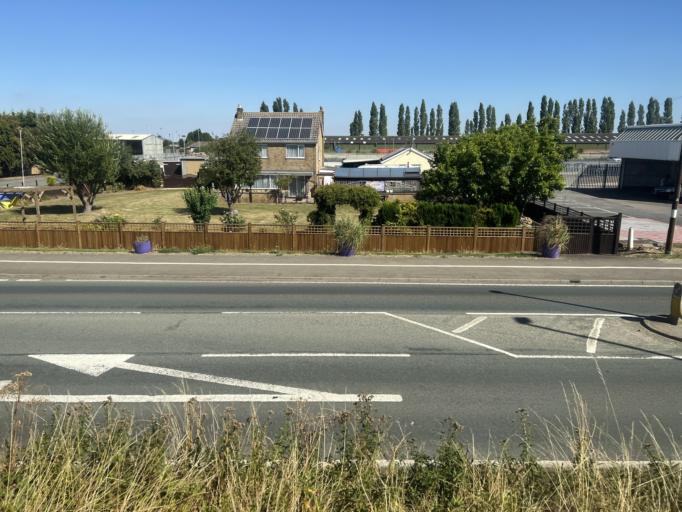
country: GB
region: England
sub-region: Lincolnshire
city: Boston
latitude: 52.9728
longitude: -0.0669
